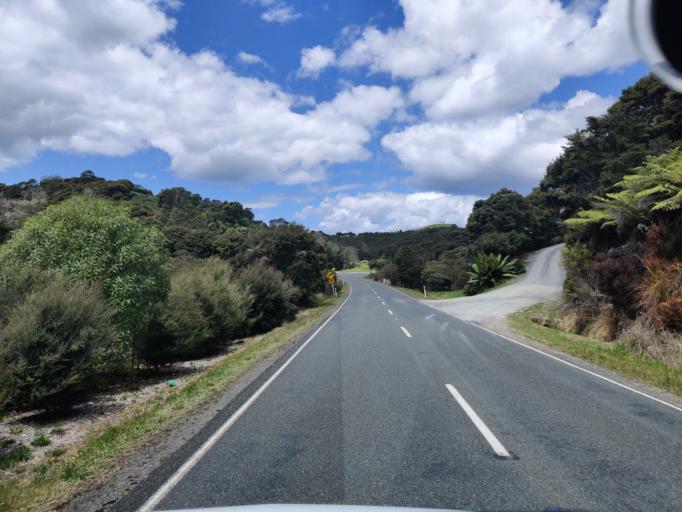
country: NZ
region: Northland
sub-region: Far North District
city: Paihia
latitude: -35.2727
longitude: 174.1380
